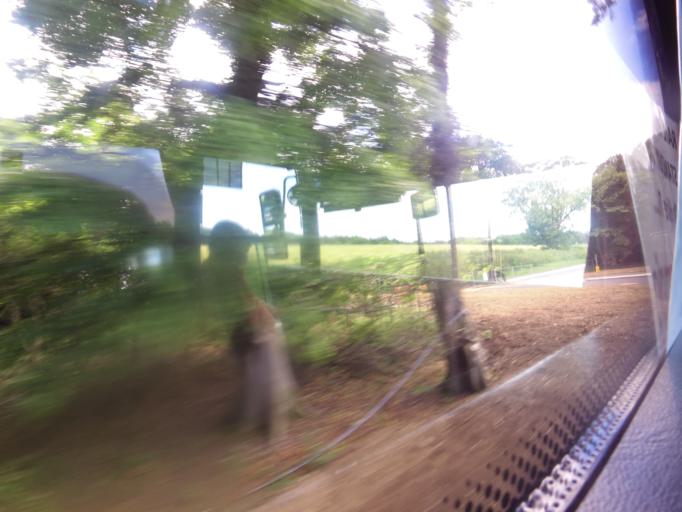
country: GB
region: England
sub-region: Norfolk
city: Sheringham
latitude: 52.9233
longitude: 1.2029
